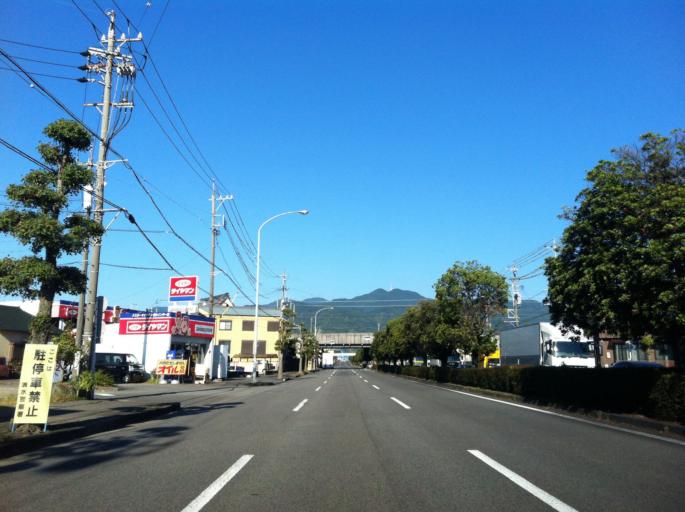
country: JP
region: Shizuoka
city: Shizuoka-shi
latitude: 35.0373
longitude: 138.4905
